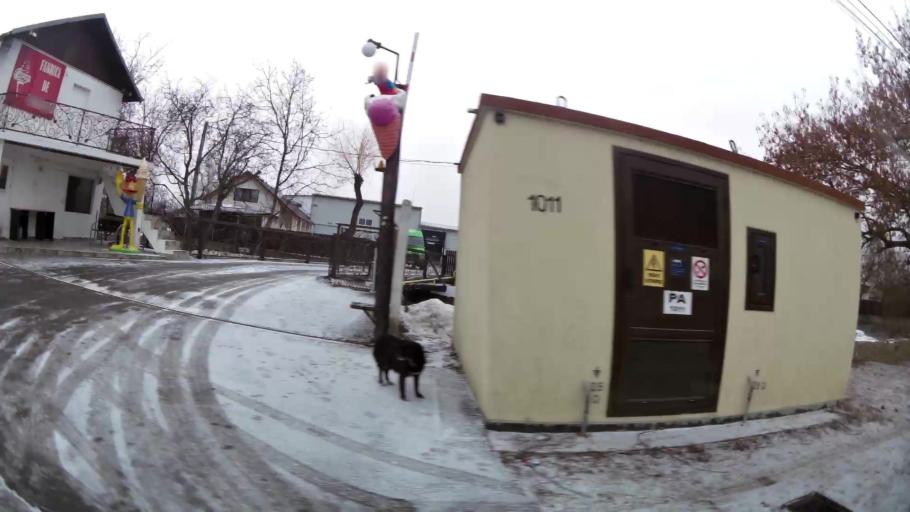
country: RO
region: Dambovita
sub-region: Municipiul Targoviste
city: Targoviste
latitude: 44.9299
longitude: 25.4775
